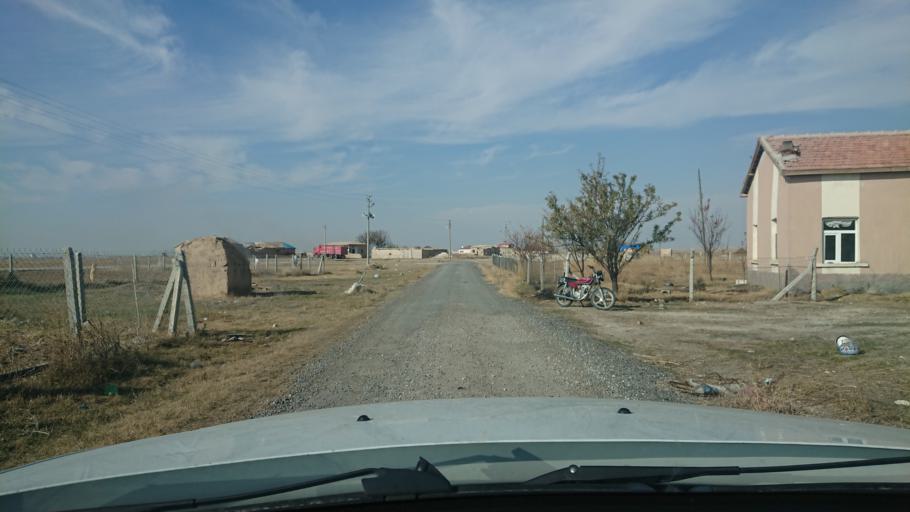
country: TR
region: Aksaray
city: Sultanhani
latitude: 38.2573
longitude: 33.4766
